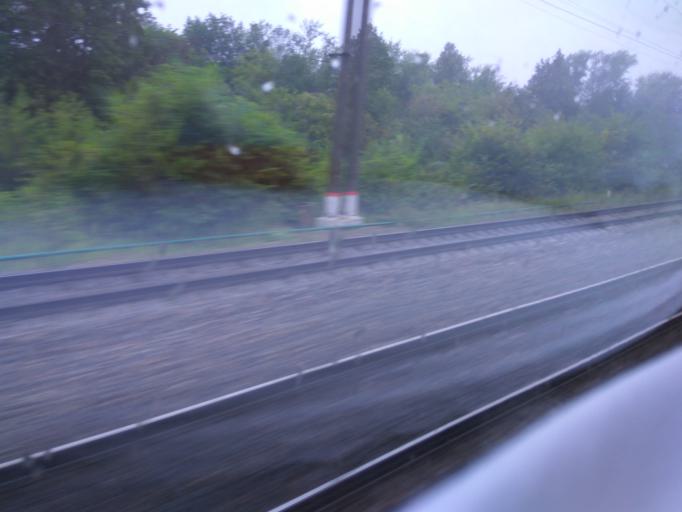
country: RU
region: Moskovskaya
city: Uzunovo
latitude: 54.6767
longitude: 38.5327
